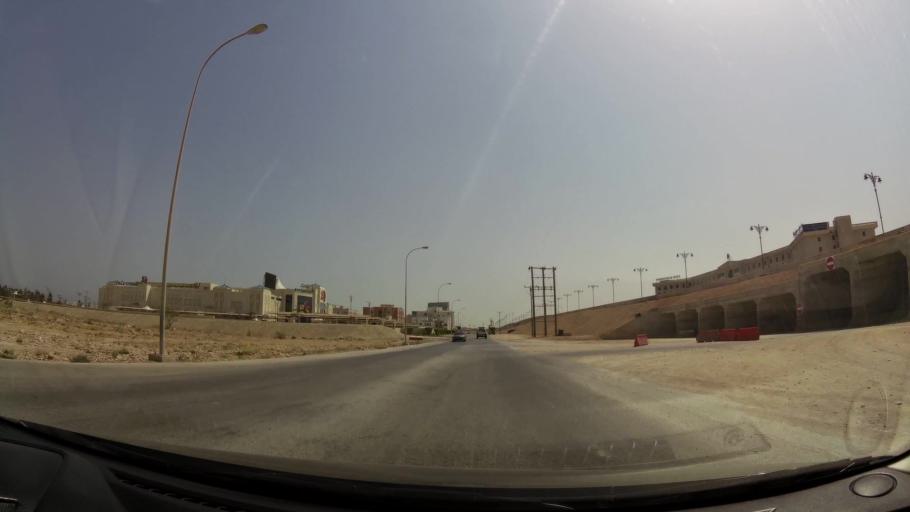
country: OM
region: Zufar
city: Salalah
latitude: 17.0192
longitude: 54.0629
